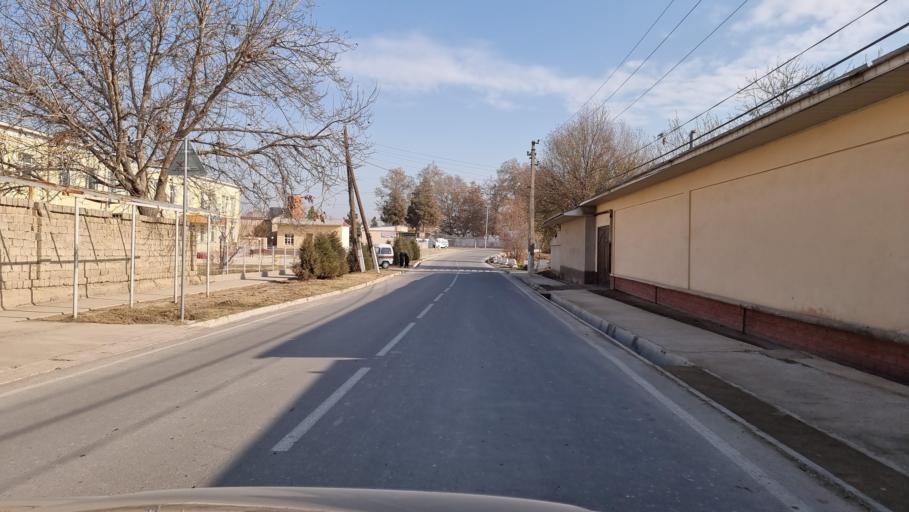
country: UZ
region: Toshkent
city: Urtaowul
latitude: 41.1898
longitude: 69.1256
